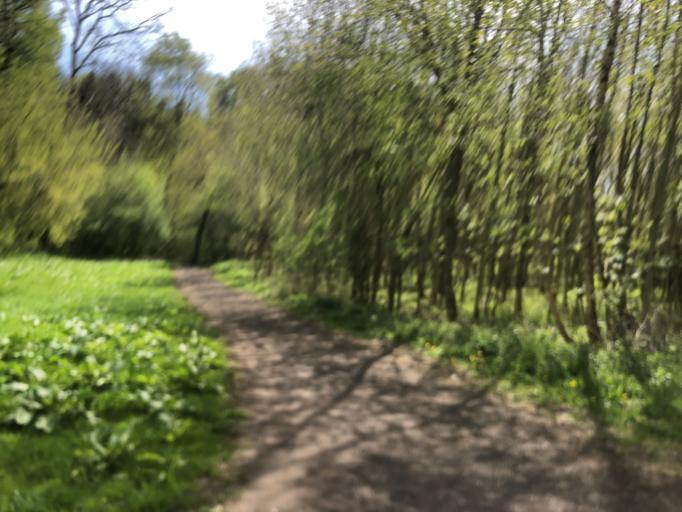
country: DK
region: Zealand
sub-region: Ringsted Kommune
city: Ringsted
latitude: 55.4510
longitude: 11.8287
